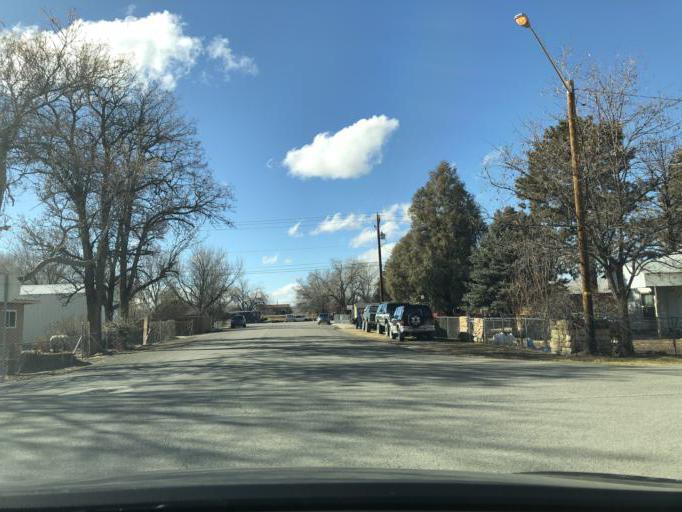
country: US
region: Utah
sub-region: Carbon County
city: East Carbon City
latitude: 38.9938
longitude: -110.1608
